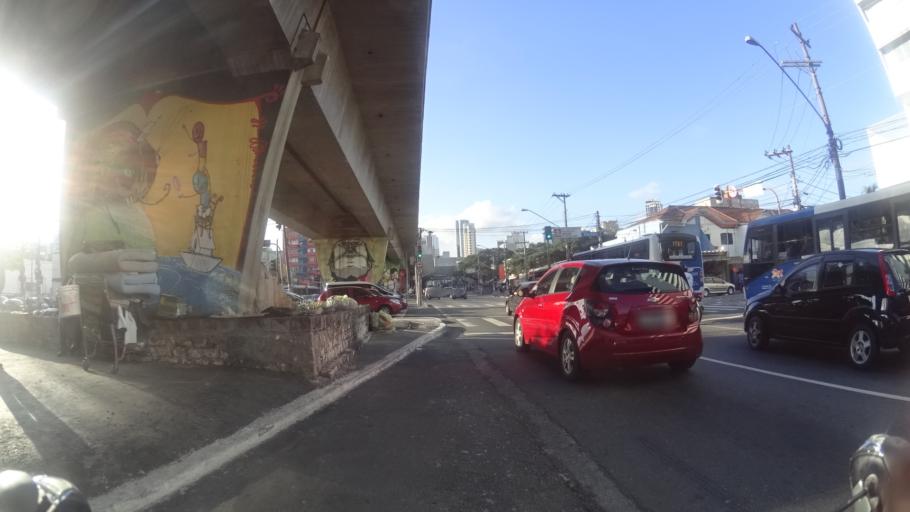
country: BR
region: Sao Paulo
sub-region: Sao Paulo
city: Sao Paulo
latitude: -23.5045
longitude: -46.6247
